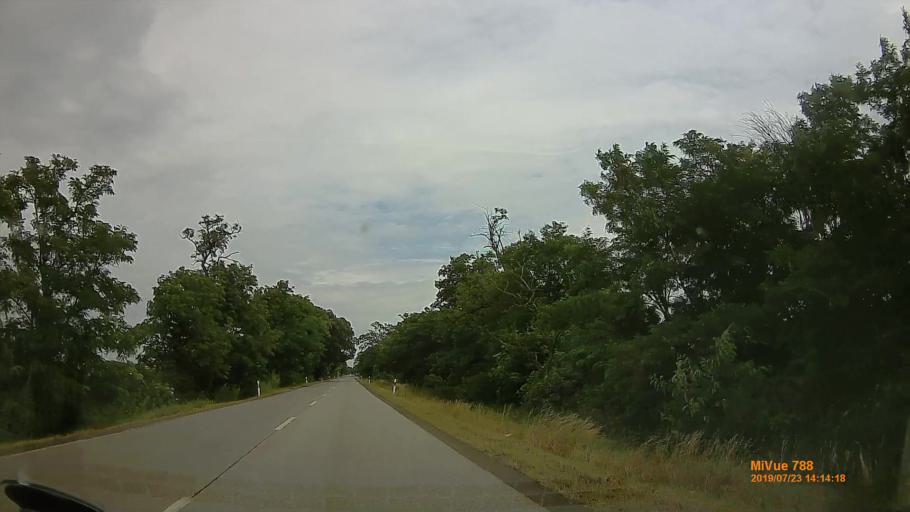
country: HU
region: Szabolcs-Szatmar-Bereg
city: Nagycserkesz
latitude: 47.9575
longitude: 21.4904
